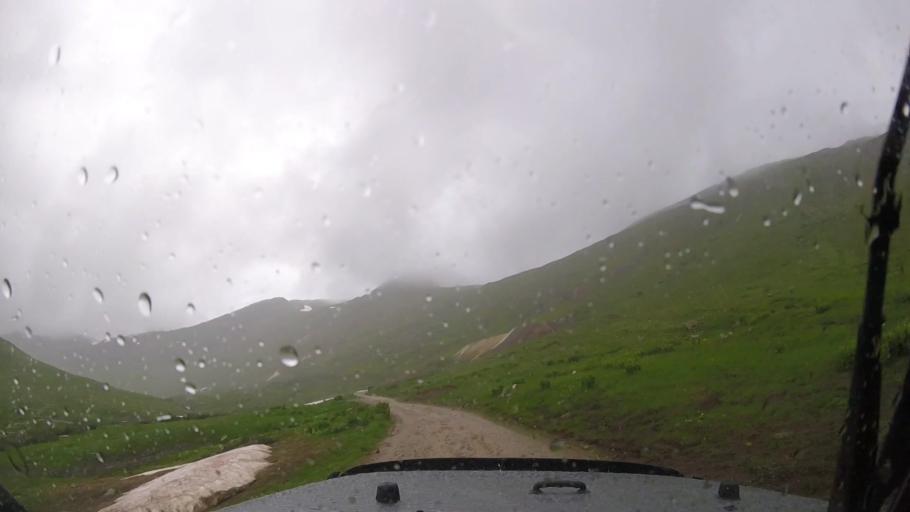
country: US
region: Colorado
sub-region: Ouray County
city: Ouray
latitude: 37.9329
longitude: -107.5947
